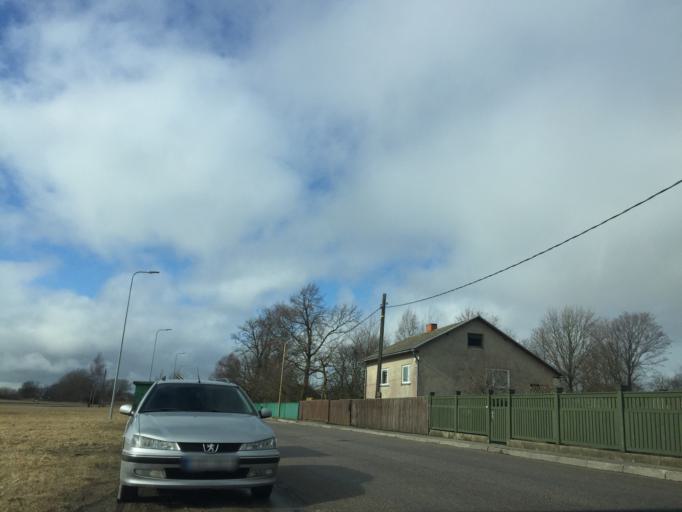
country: EE
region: Laeaene
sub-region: Haapsalu linn
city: Haapsalu
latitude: 58.9528
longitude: 23.5243
